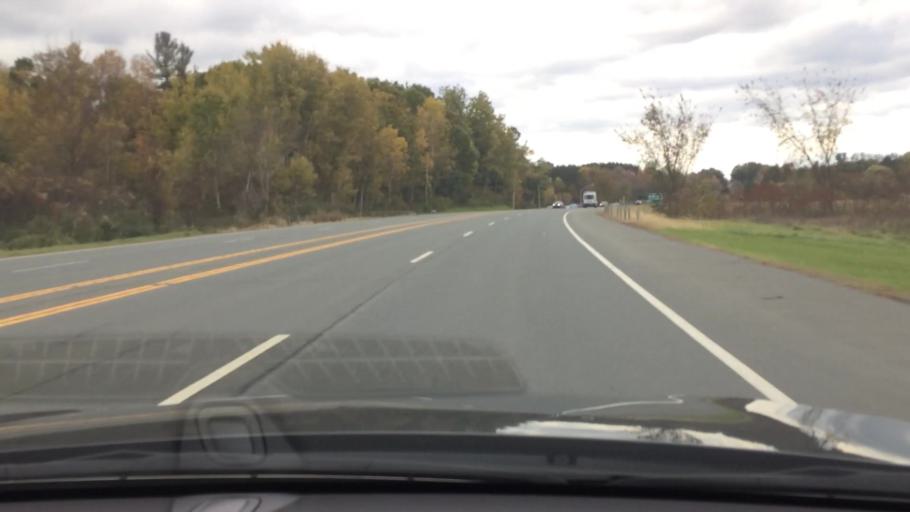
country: US
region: New York
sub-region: Columbia County
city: Niverville
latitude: 42.4780
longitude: -73.6808
